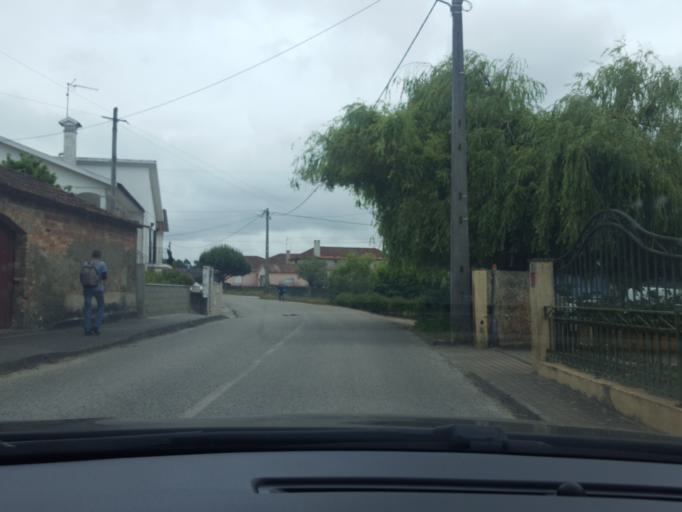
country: PT
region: Leiria
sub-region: Leiria
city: Caranguejeira
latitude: 39.7945
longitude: -8.7524
